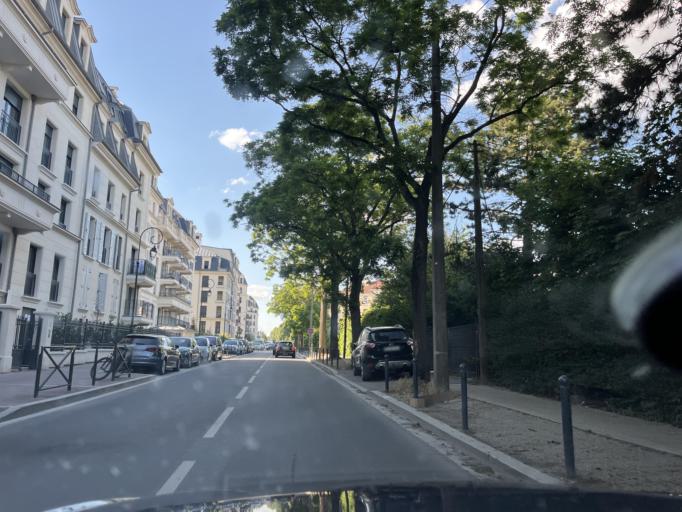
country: FR
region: Ile-de-France
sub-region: Departement des Hauts-de-Seine
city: Le Plessis-Robinson
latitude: 48.7914
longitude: 2.2729
